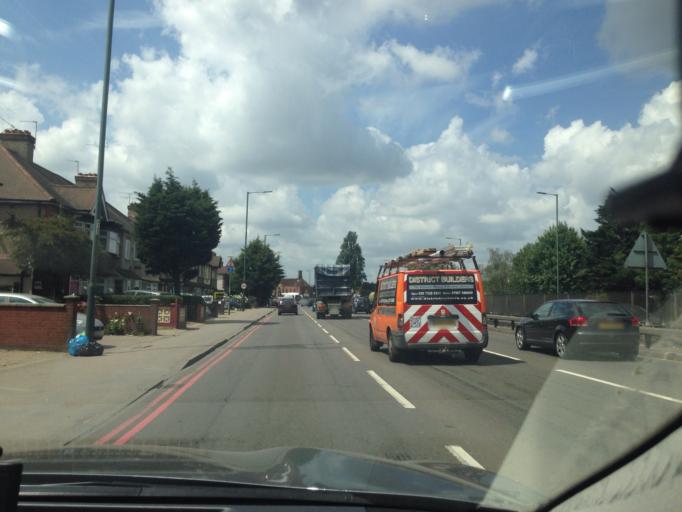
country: GB
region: England
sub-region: Greater London
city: Wembley
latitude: 51.5523
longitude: -0.2579
